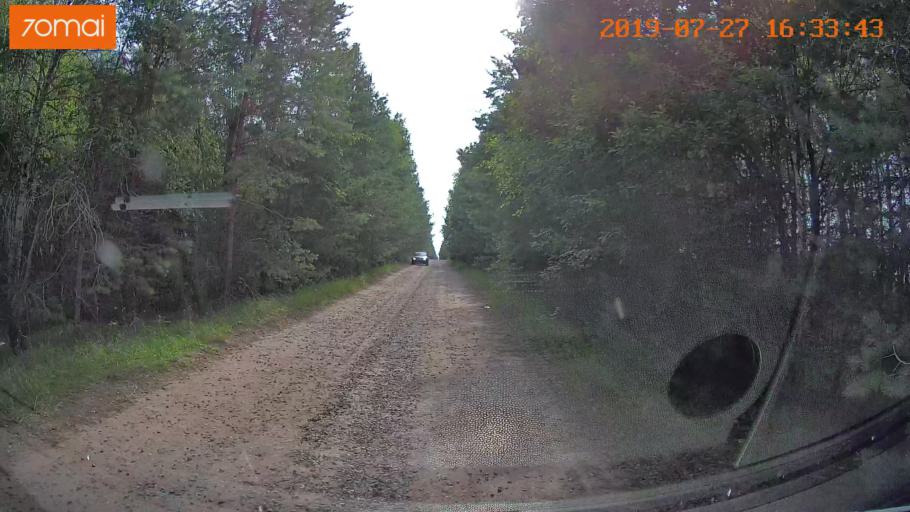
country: RU
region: Ivanovo
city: Novo-Talitsy
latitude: 57.0881
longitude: 40.8498
